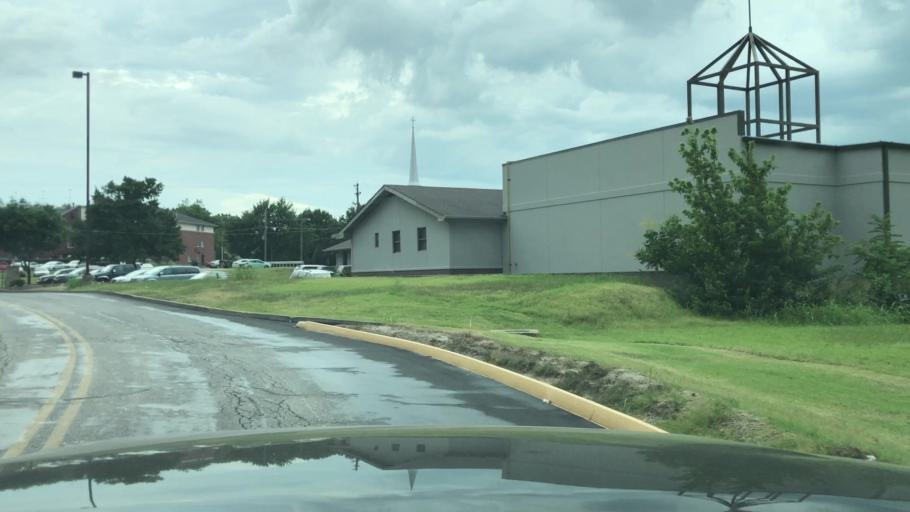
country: US
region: Missouri
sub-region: Saint Charles County
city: Saint Charles
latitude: 38.7729
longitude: -90.4981
